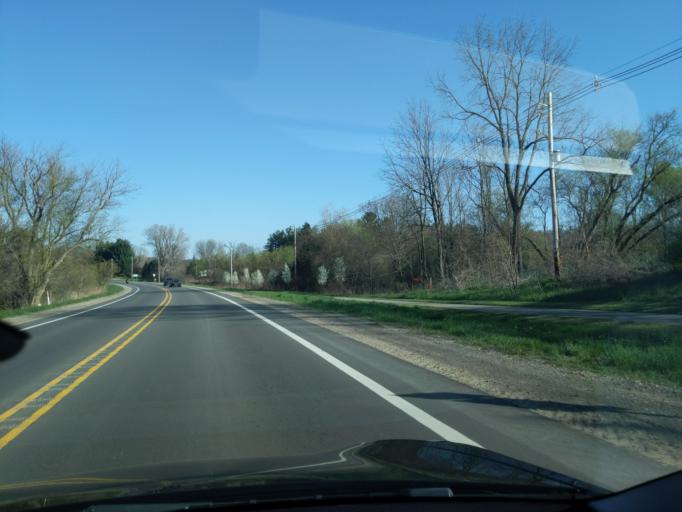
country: US
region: Michigan
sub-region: Washtenaw County
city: Chelsea
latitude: 42.3521
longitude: -84.0536
